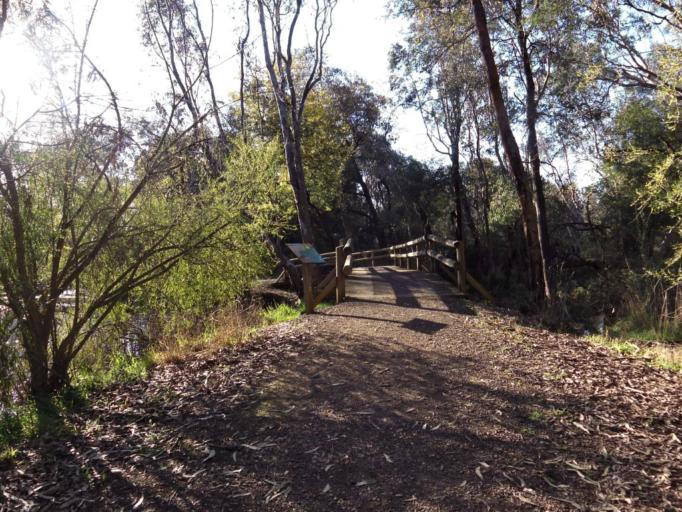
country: AU
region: Victoria
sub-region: Murrindindi
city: Alexandra
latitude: -37.2084
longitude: 145.4283
